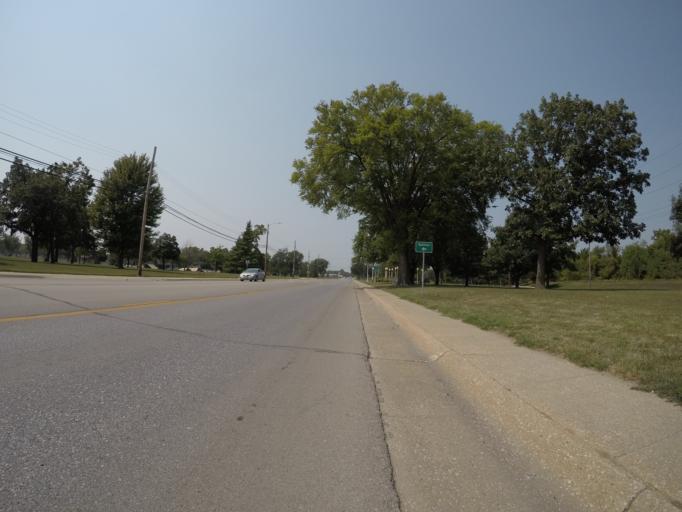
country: US
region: Nebraska
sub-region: Gage County
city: Beatrice
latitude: 40.2660
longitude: -96.7565
